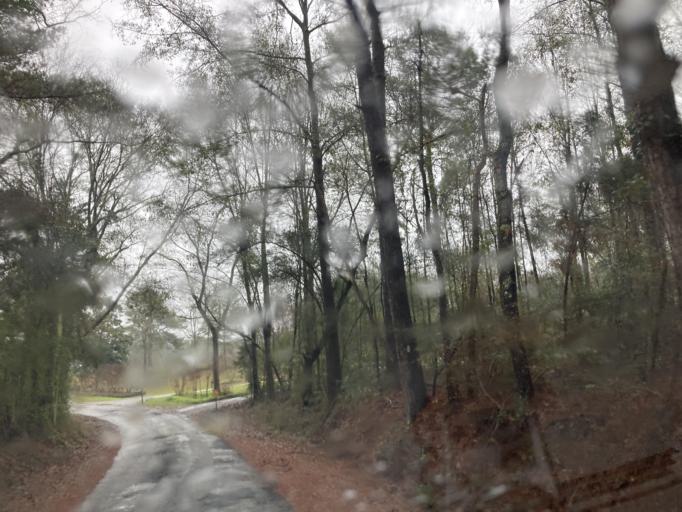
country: US
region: Mississippi
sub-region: Forrest County
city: Rawls Springs
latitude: 31.4948
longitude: -89.3405
